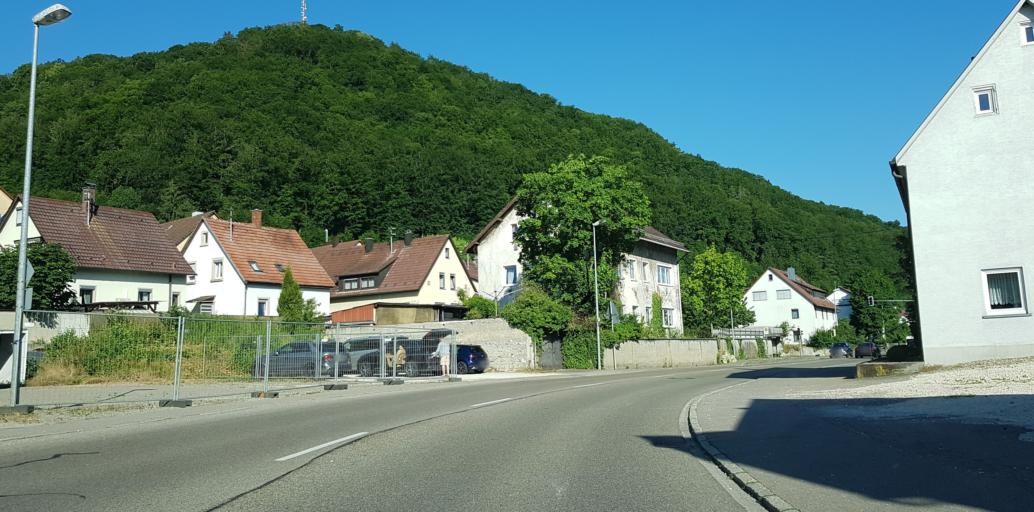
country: DE
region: Baden-Wuerttemberg
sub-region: Tuebingen Region
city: Blaubeuren
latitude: 48.3984
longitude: 9.8003
